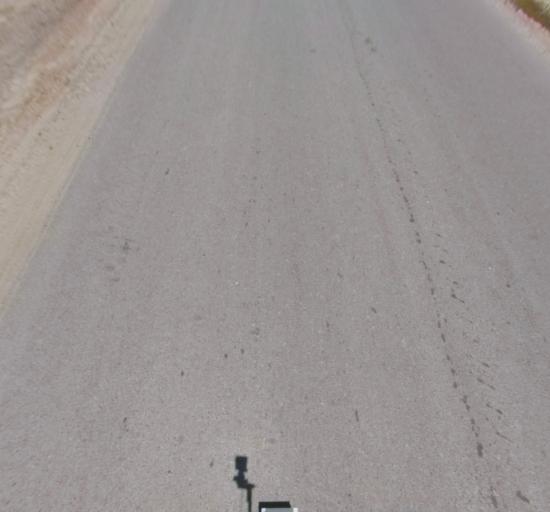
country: US
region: California
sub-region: Madera County
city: Fairmead
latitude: 36.9942
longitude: -120.2742
